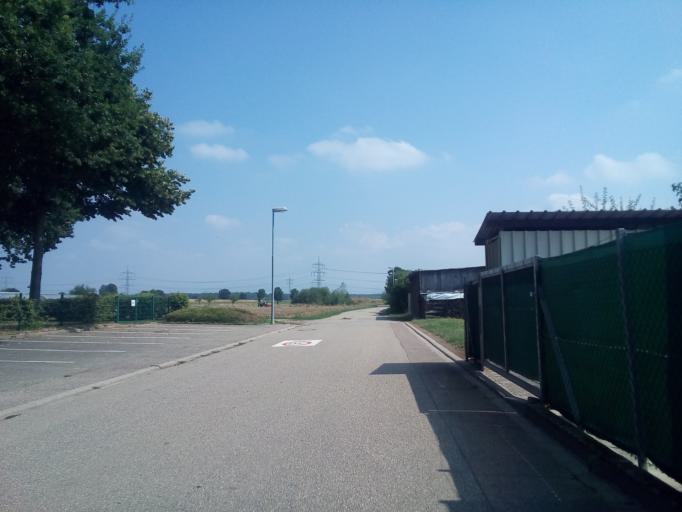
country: DE
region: Baden-Wuerttemberg
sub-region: Freiburg Region
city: Willstatt
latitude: 48.5985
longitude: 7.8768
